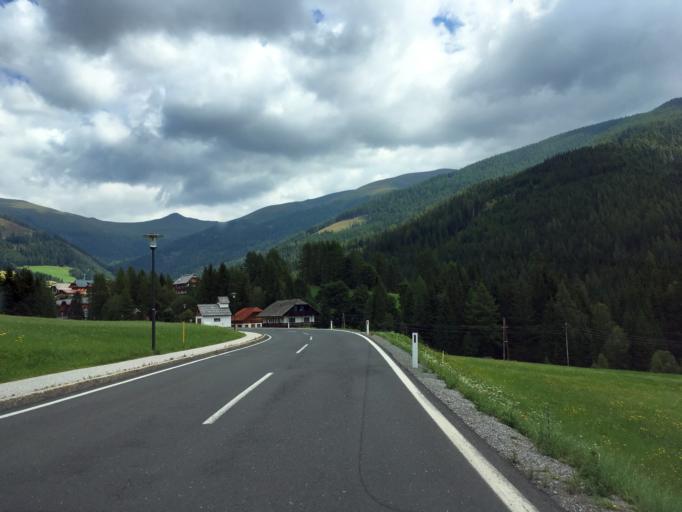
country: AT
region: Carinthia
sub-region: Politischer Bezirk Spittal an der Drau
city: Kleinkirchheim
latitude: 46.8380
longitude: 13.7637
